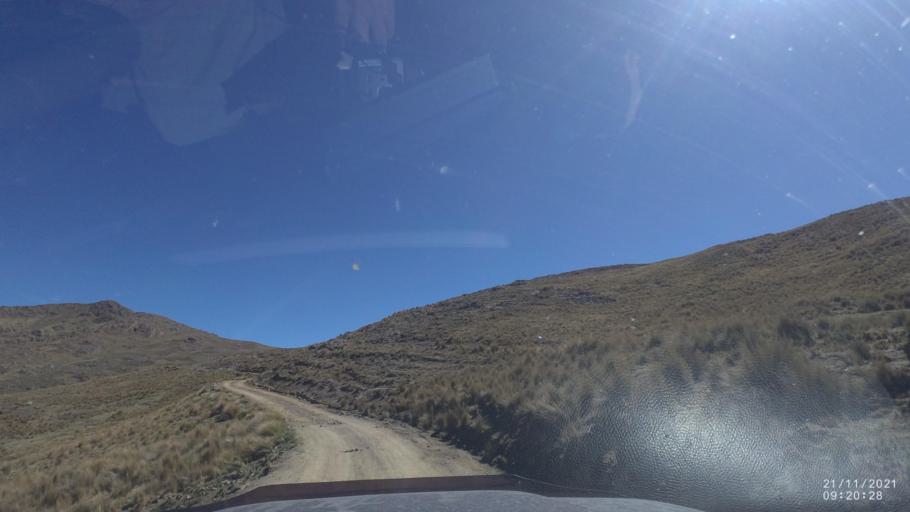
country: BO
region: Cochabamba
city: Cochabamba
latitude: -17.1099
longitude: -66.2512
